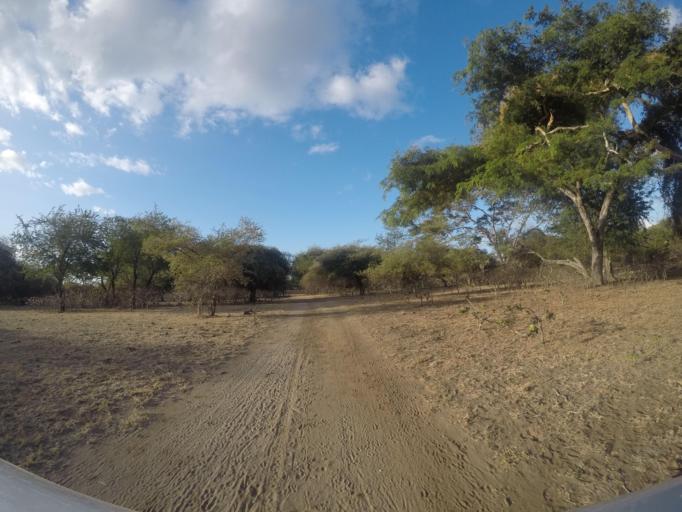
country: TL
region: Lautem
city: Lospalos
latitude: -8.3276
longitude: 126.9782
